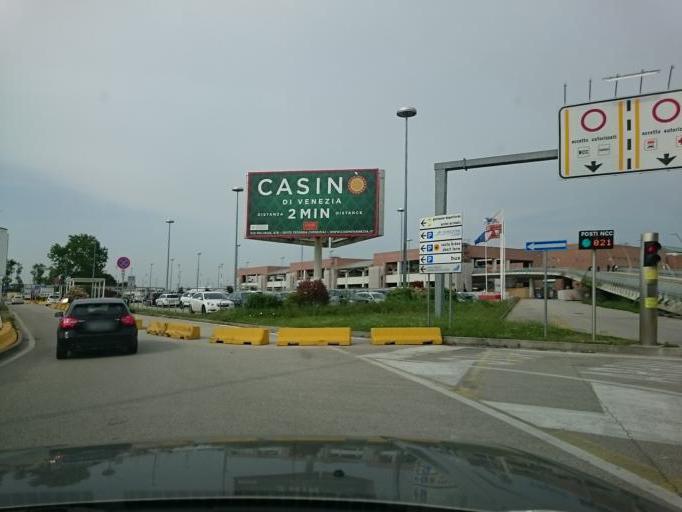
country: IT
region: Veneto
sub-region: Provincia di Venezia
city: Tessera
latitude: 45.5032
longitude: 12.3380
